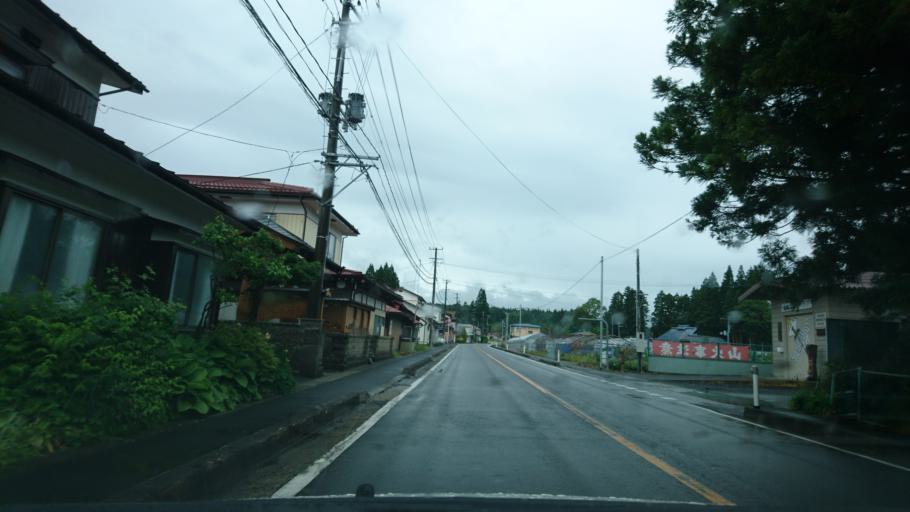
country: JP
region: Iwate
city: Ichinoseki
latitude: 38.9705
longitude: 140.9964
